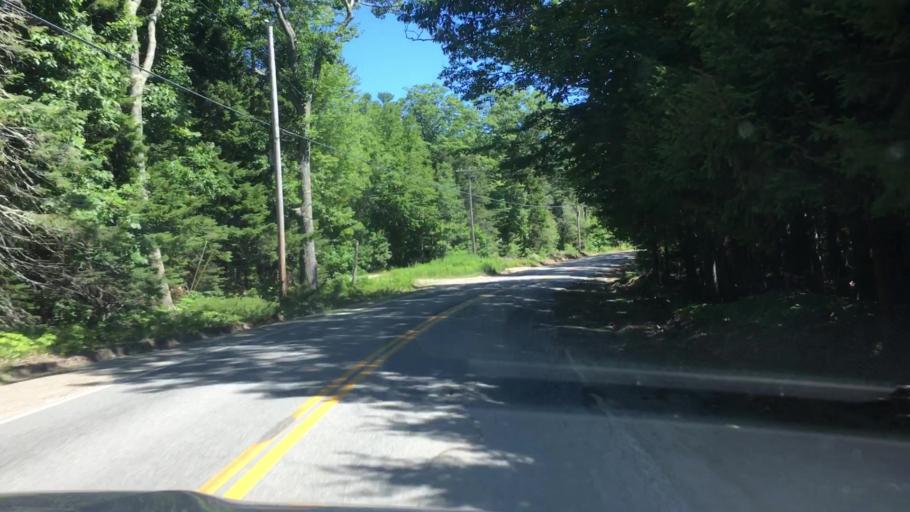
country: US
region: Maine
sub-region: Hancock County
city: Penobscot
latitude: 44.4374
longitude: -68.7117
